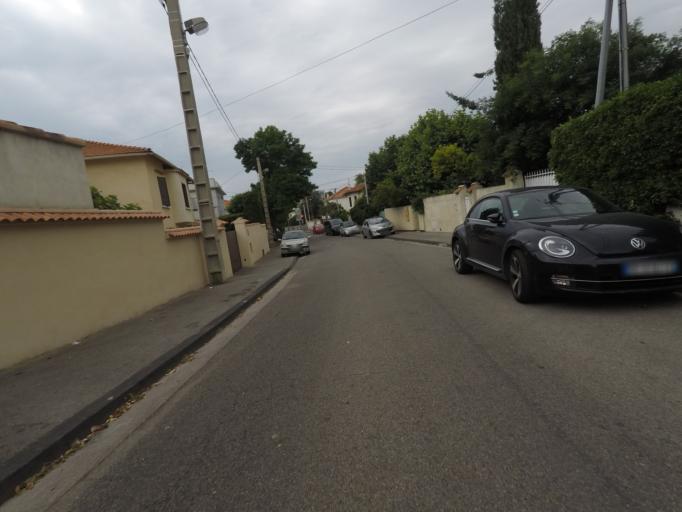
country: FR
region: Provence-Alpes-Cote d'Azur
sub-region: Departement des Bouches-du-Rhone
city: Marseille 08
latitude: 43.2614
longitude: 5.3885
